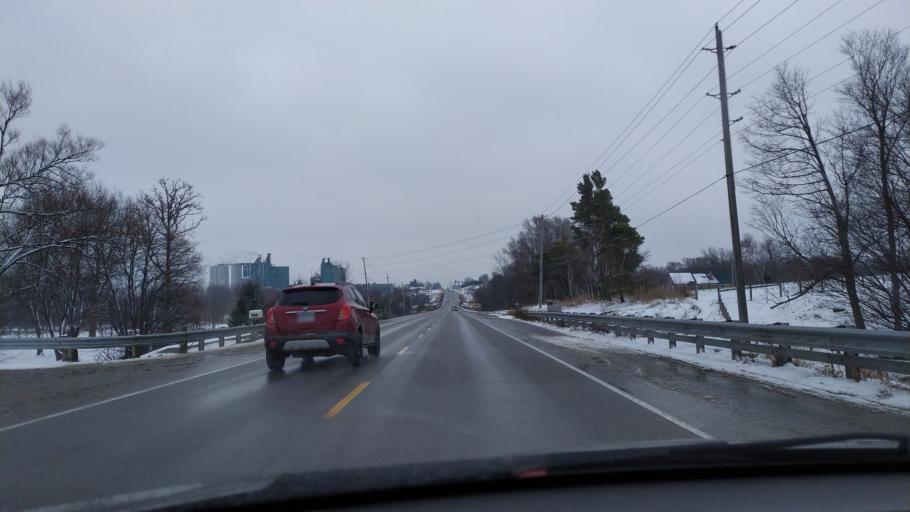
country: CA
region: Ontario
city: Waterloo
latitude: 43.6046
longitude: -80.6471
